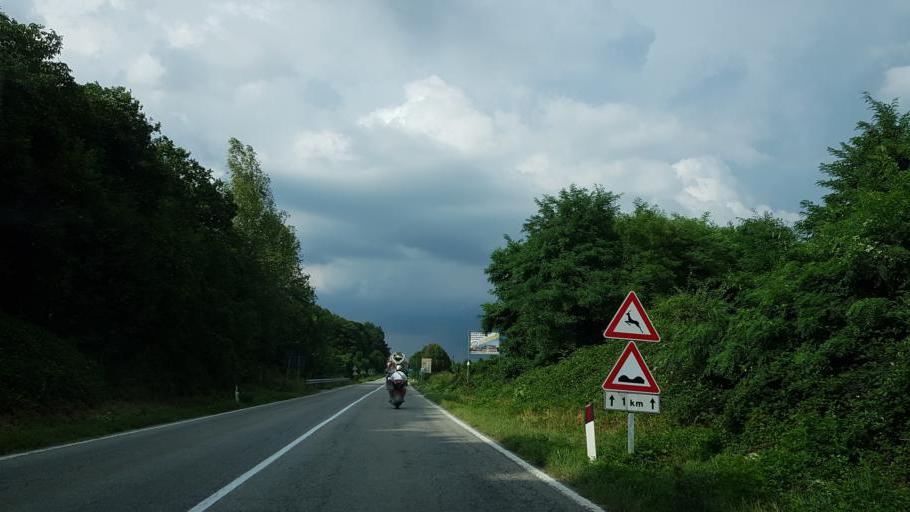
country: IT
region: Piedmont
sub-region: Provincia di Cuneo
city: Vignolo
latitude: 44.3505
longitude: 7.4767
